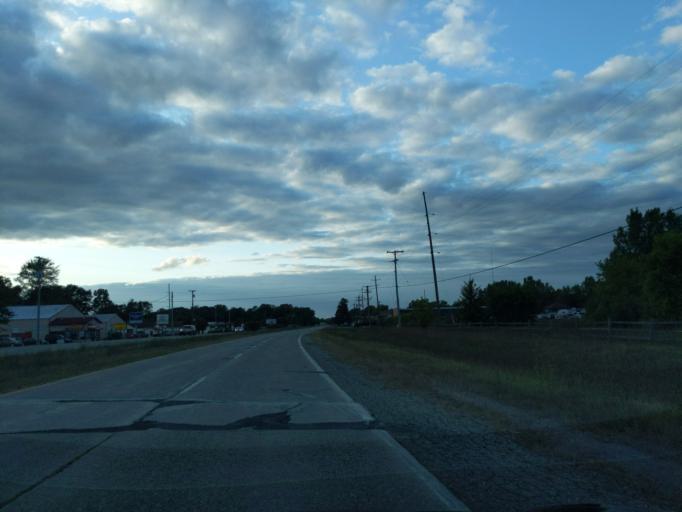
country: US
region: Michigan
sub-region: Ingham County
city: Holt
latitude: 42.6168
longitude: -84.4971
